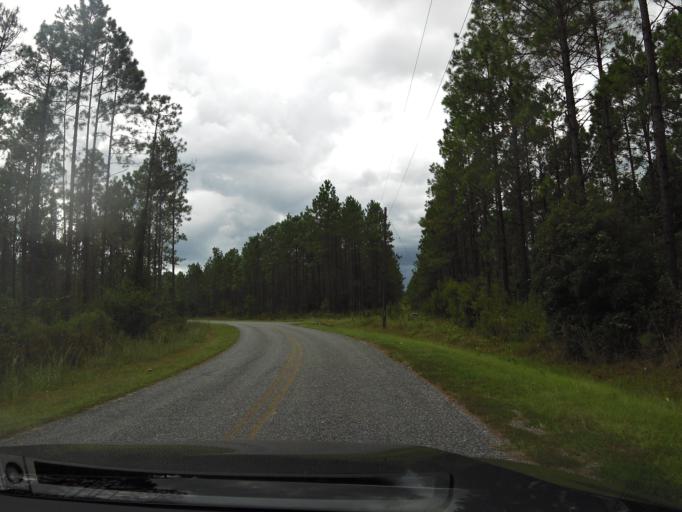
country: US
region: Georgia
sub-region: Brantley County
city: Nahunta
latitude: 31.2056
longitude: -81.9946
